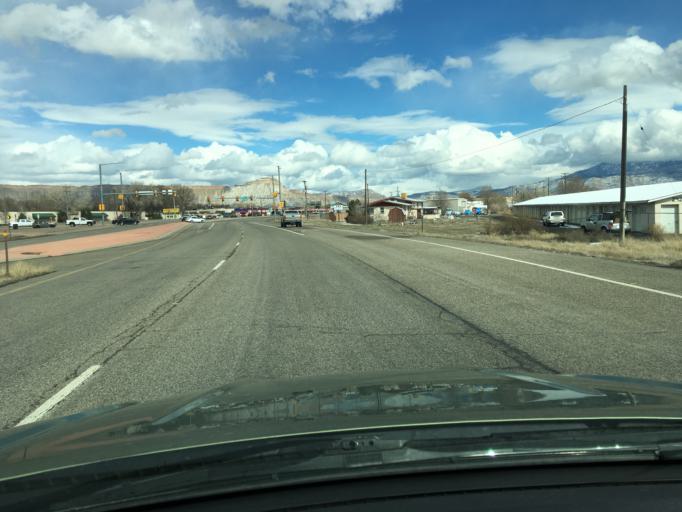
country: US
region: Colorado
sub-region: Mesa County
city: Fruitvale
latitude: 39.0762
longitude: -108.5012
